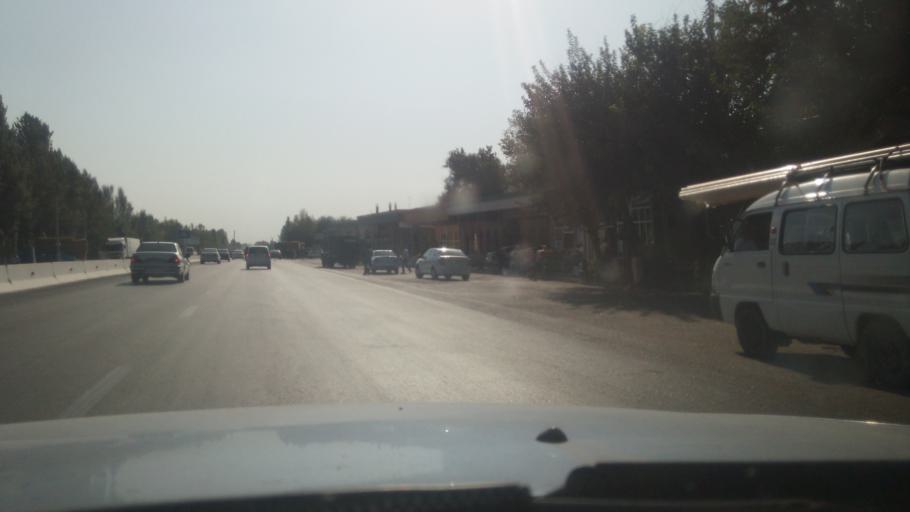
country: UZ
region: Toshkent
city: Urtaowul
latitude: 41.2193
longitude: 69.1340
